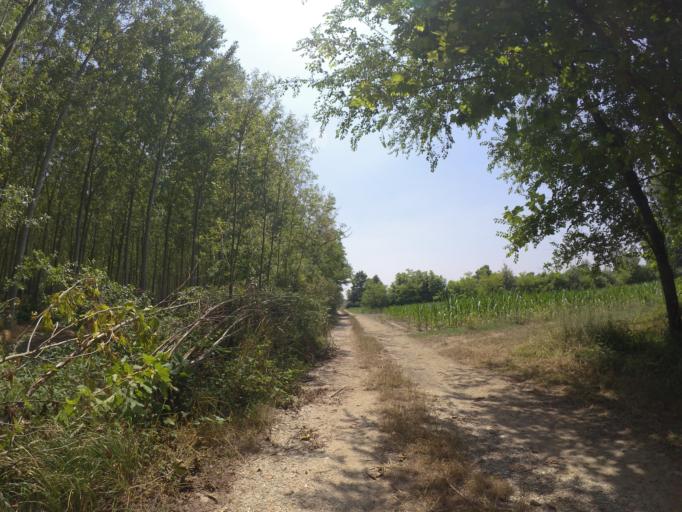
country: IT
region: Friuli Venezia Giulia
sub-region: Provincia di Udine
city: Bertiolo
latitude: 45.9250
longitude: 13.0535
